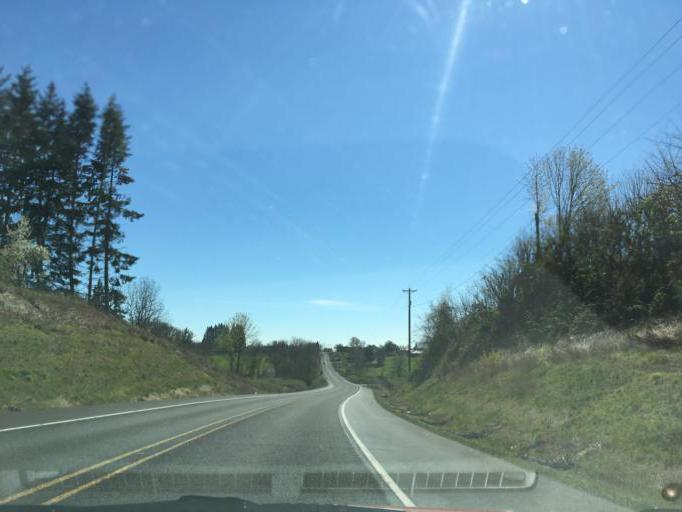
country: US
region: Oregon
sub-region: Clackamas County
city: Canby
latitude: 45.1958
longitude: -122.7226
